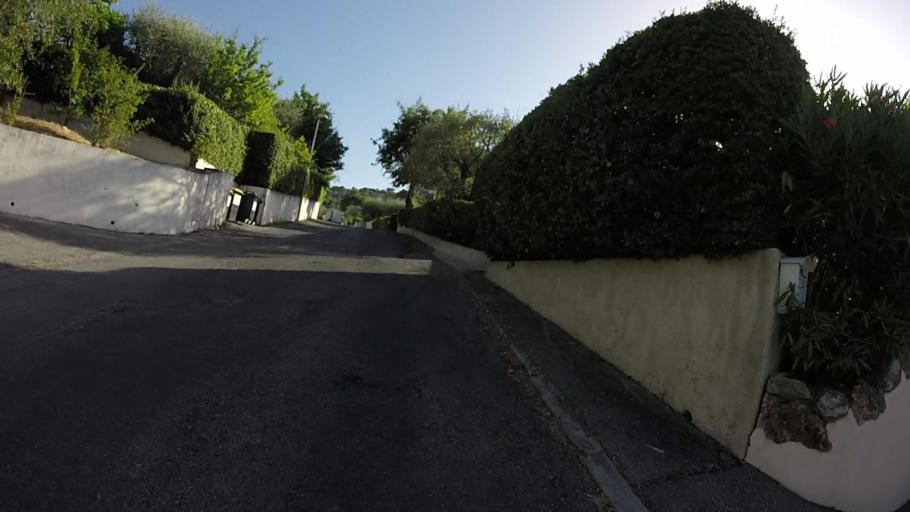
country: FR
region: Provence-Alpes-Cote d'Azur
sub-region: Departement des Alpes-Maritimes
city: Mouans-Sartoux
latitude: 43.6275
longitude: 6.9766
